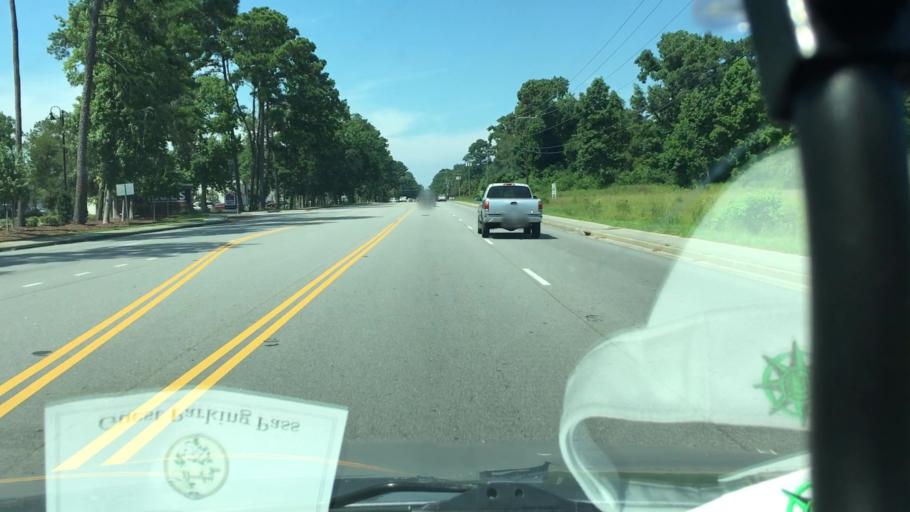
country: US
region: South Carolina
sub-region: Beaufort County
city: Burton
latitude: 32.4305
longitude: -80.7178
